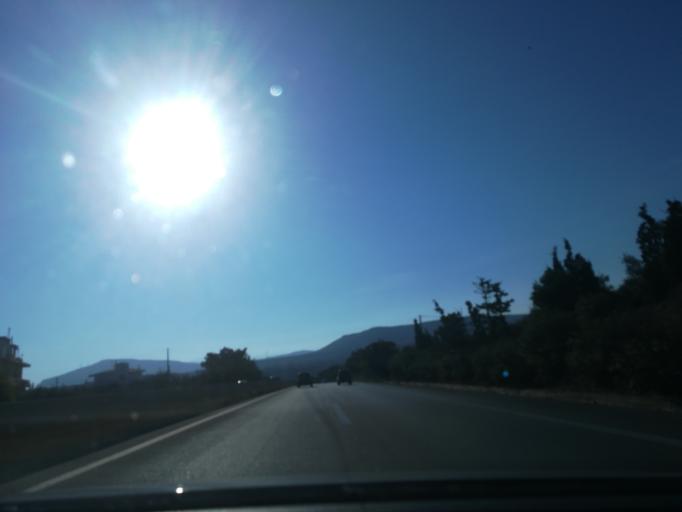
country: GR
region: Crete
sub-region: Nomos Irakleiou
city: Gournes
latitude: 35.3267
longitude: 25.2739
